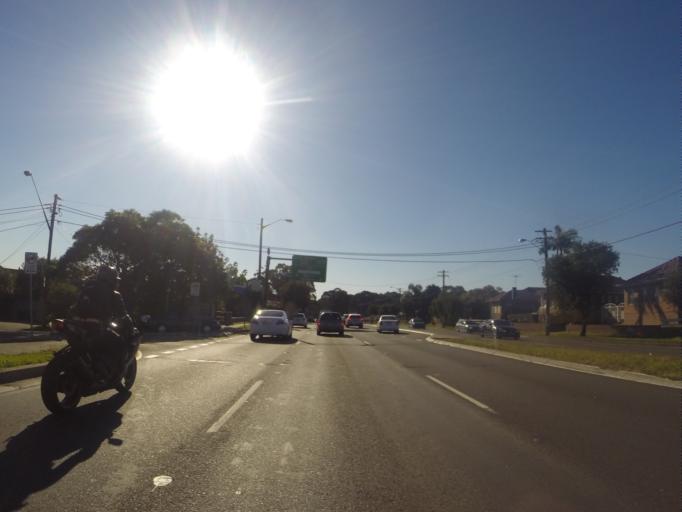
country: AU
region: New South Wales
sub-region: Canterbury
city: Roselands
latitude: -33.9314
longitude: 151.0728
